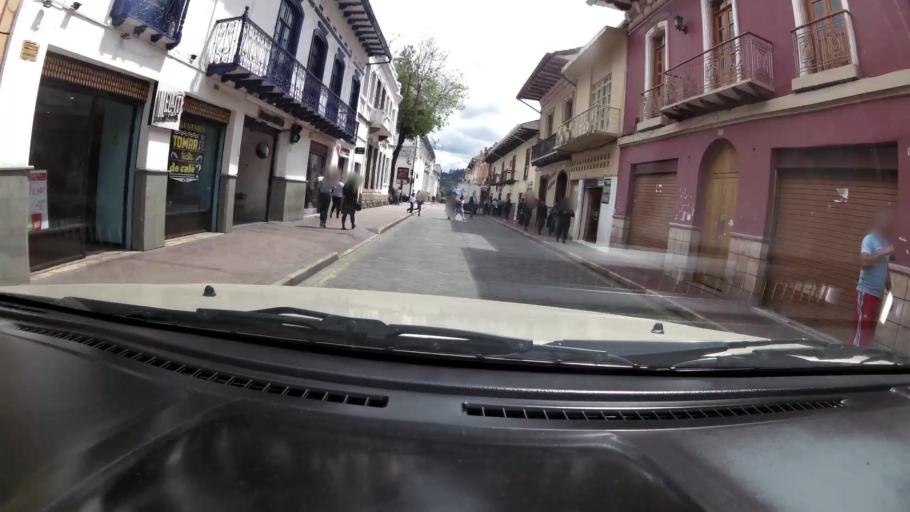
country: EC
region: Azuay
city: Cuenca
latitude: -2.8988
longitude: -79.0033
